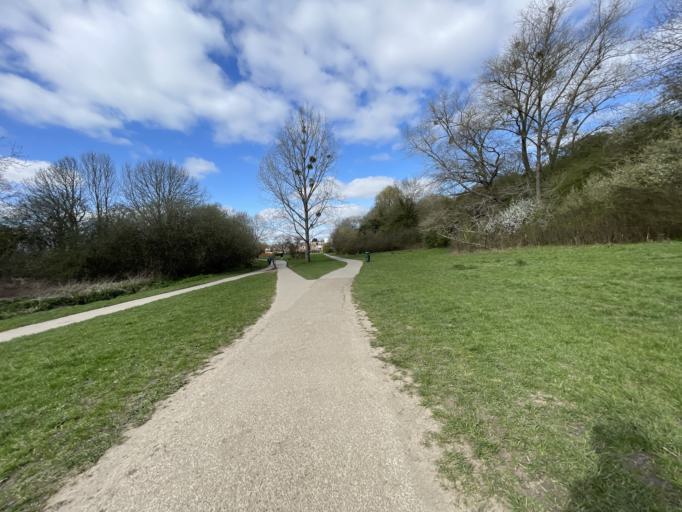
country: GB
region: England
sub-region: Greater London
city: Barnet
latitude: 51.6383
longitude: -0.1861
